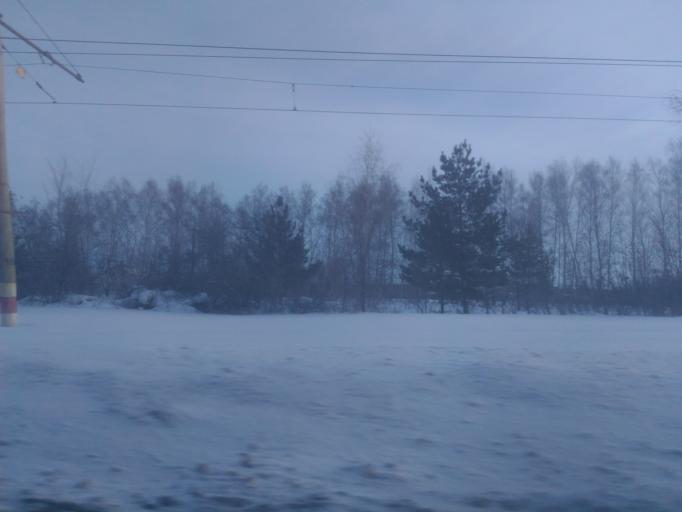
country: RU
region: Ulyanovsk
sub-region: Ulyanovskiy Rayon
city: Ulyanovsk
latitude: 54.3675
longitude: 48.3189
